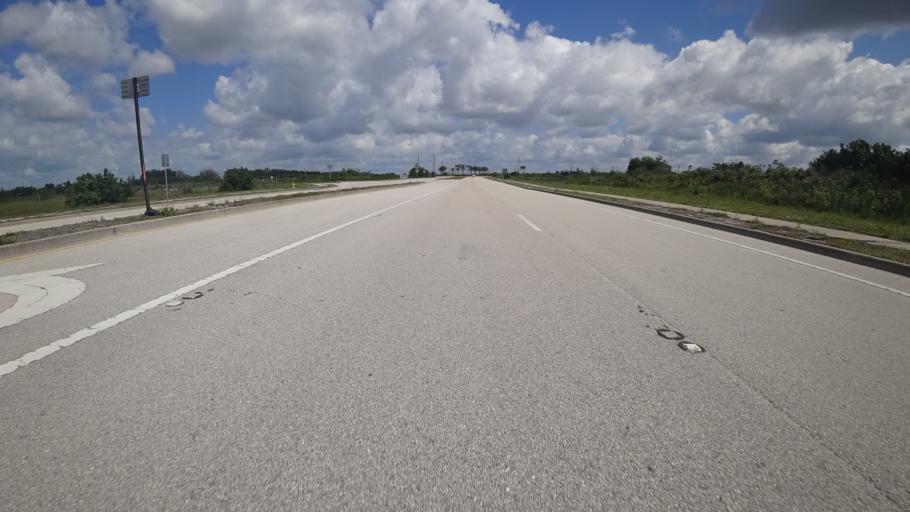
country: US
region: Florida
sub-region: Manatee County
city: Longboat Key
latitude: 27.4454
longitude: -82.6369
